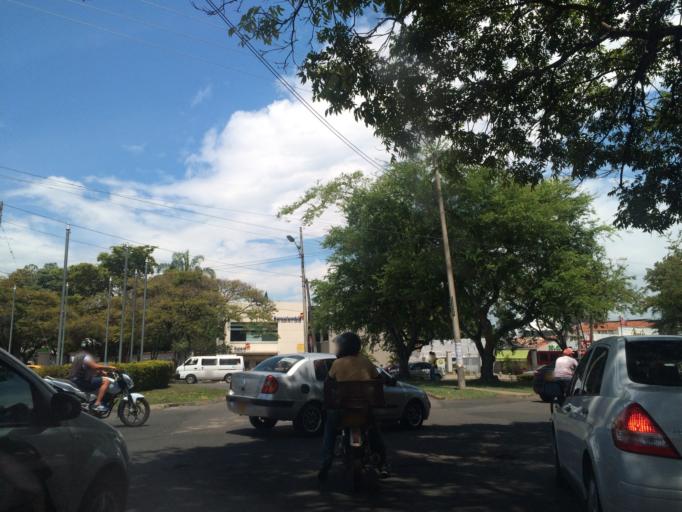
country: CO
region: Valle del Cauca
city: Cali
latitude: 3.3639
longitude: -76.5322
